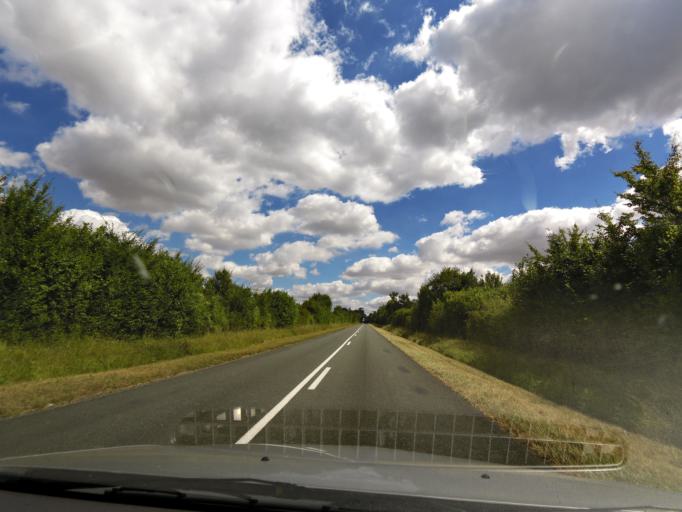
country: FR
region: Poitou-Charentes
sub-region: Departement des Deux-Sevres
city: Beauvoir-sur-Niort
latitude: 46.1522
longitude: -0.4056
